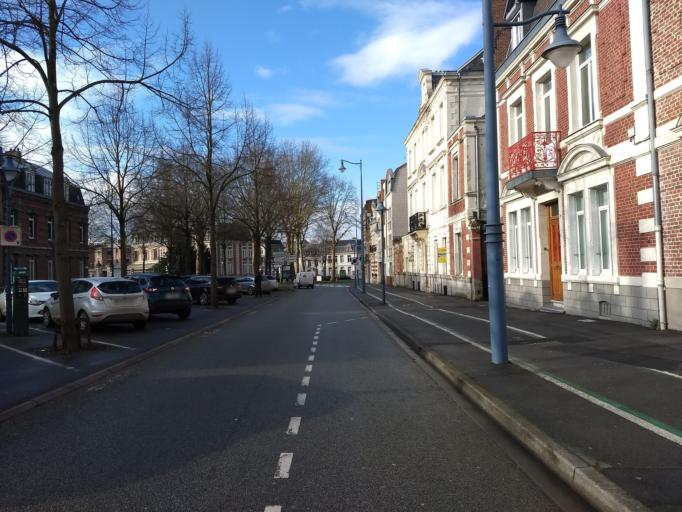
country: FR
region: Nord-Pas-de-Calais
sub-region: Departement du Pas-de-Calais
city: Arras
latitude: 50.2877
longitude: 2.7728
